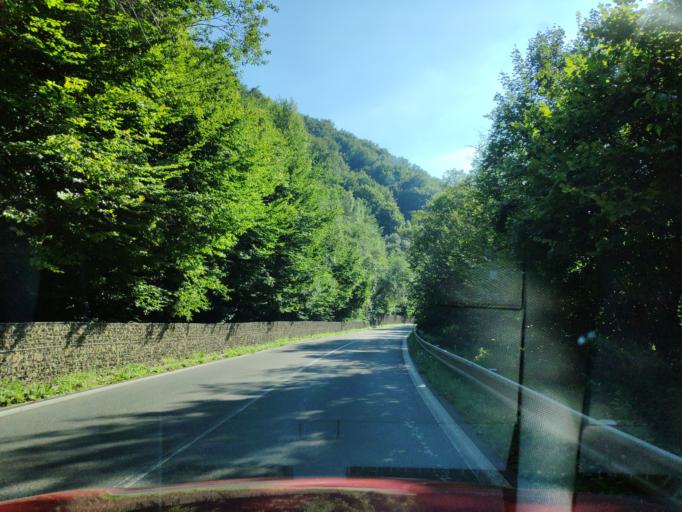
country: SK
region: Presovsky
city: Snina
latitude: 49.0389
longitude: 22.2610
